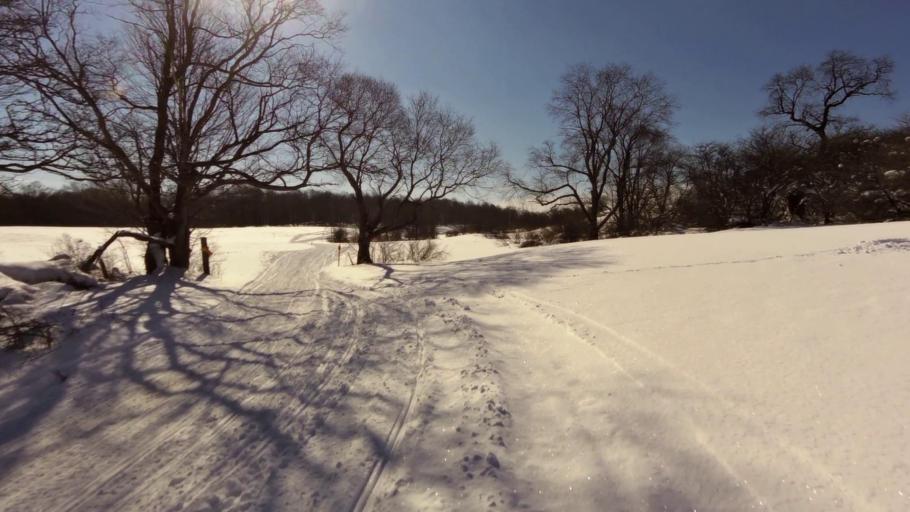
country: US
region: New York
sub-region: Cattaraugus County
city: Franklinville
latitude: 42.3973
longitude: -78.4950
